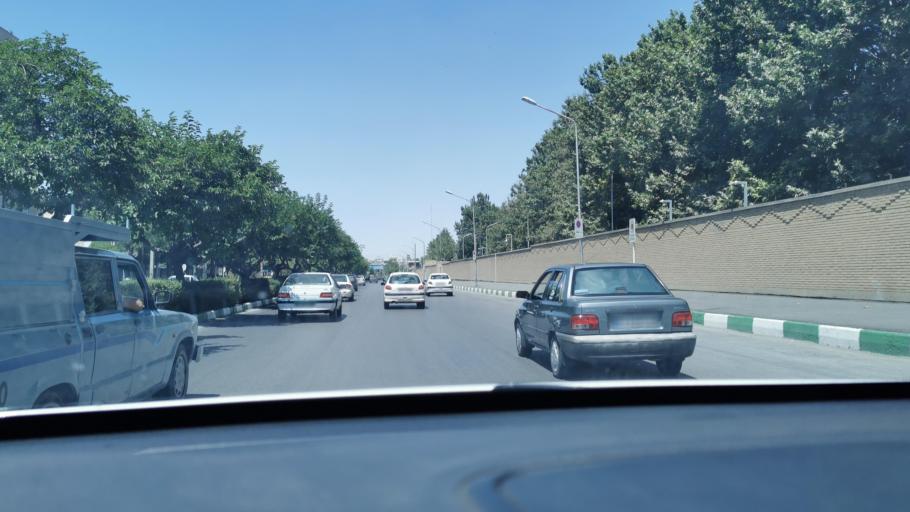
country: IR
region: Razavi Khorasan
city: Mashhad
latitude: 36.3352
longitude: 59.4870
